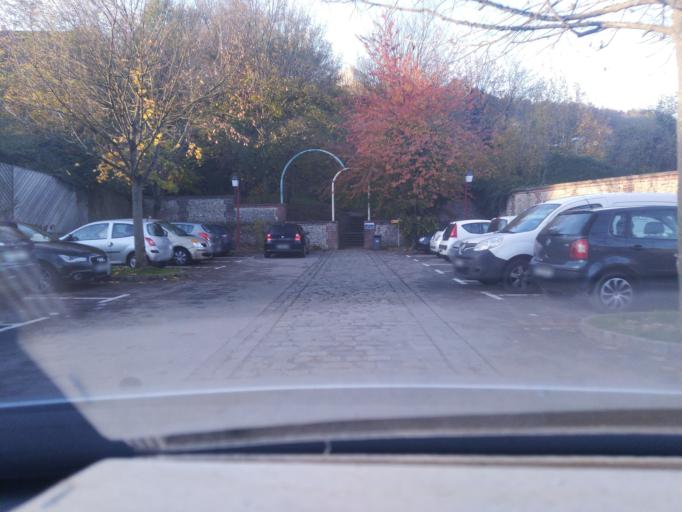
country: FR
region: Haute-Normandie
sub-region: Departement de la Seine-Maritime
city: Darnetal
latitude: 49.4407
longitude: 1.1445
